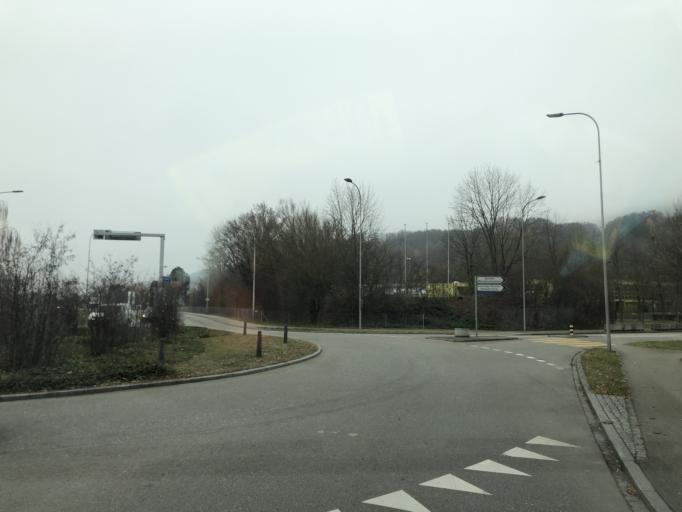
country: CH
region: Aargau
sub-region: Bezirk Baden
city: Obersiggenthal
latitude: 47.4894
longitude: 8.2856
